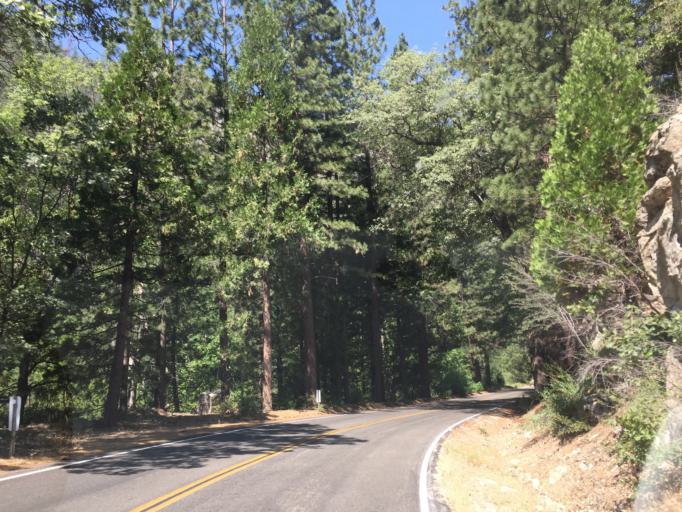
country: US
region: California
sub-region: Tulare County
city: Three Rivers
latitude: 36.8024
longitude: -118.7453
